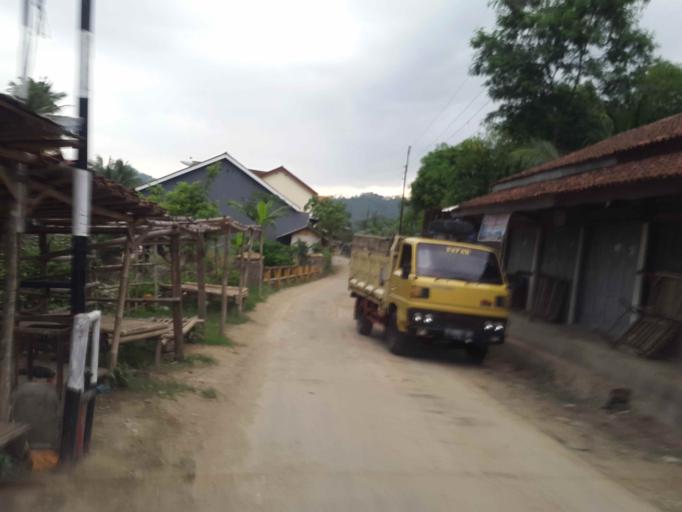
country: ID
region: Central Java
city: Bantarmangu
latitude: -7.3465
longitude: 108.8912
